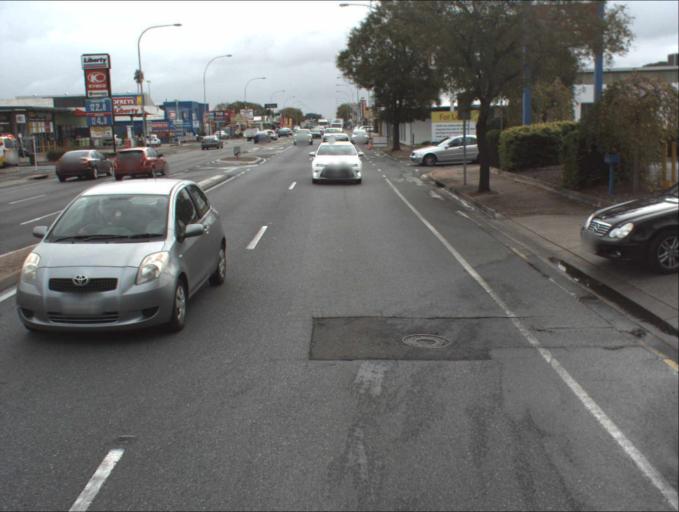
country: AU
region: South Australia
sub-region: Prospect
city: Prospect
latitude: -34.8891
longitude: 138.6031
